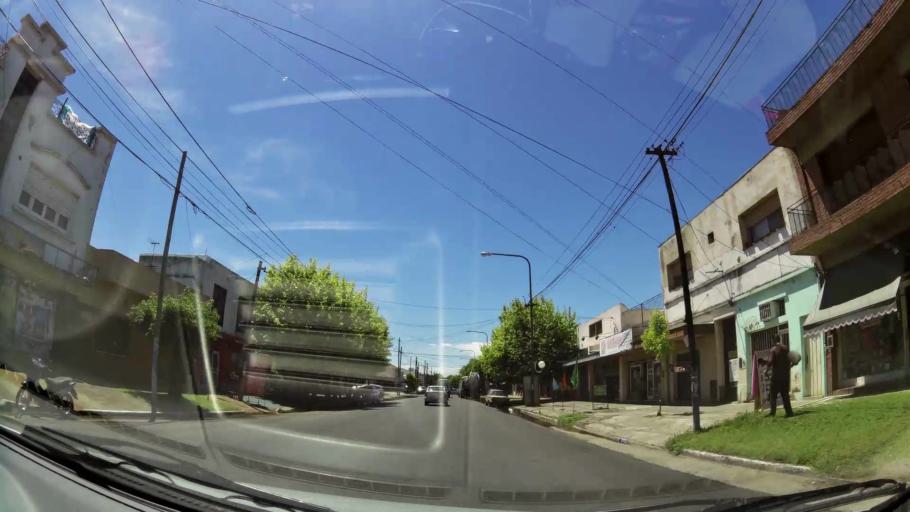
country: AR
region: Buenos Aires
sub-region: Partido de Quilmes
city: Quilmes
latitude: -34.7249
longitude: -58.2732
